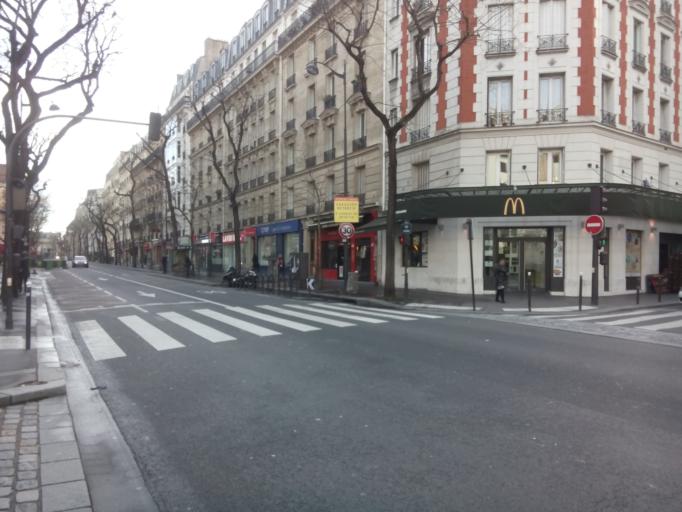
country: FR
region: Ile-de-France
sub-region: Departement du Val-de-Marne
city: Le Kremlin-Bicetre
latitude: 48.8270
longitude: 2.3665
